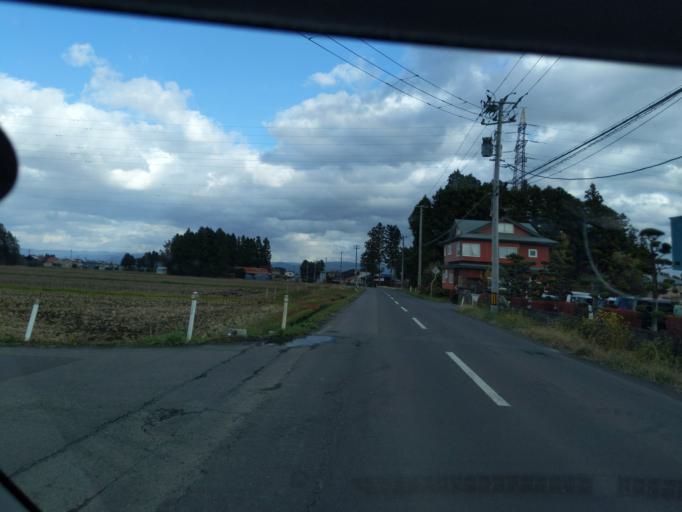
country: JP
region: Iwate
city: Mizusawa
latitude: 39.1265
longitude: 141.0840
